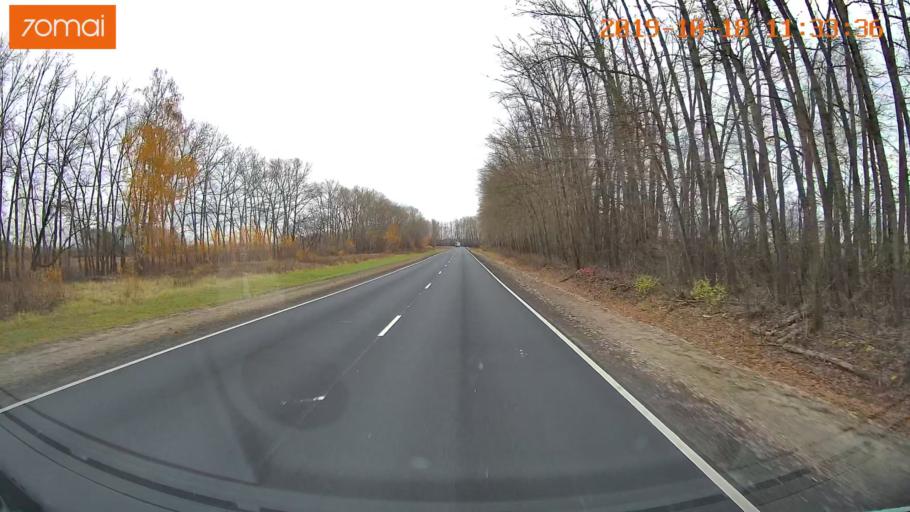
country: RU
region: Rjazan
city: Oktyabr'skiy
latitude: 54.1397
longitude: 38.7446
